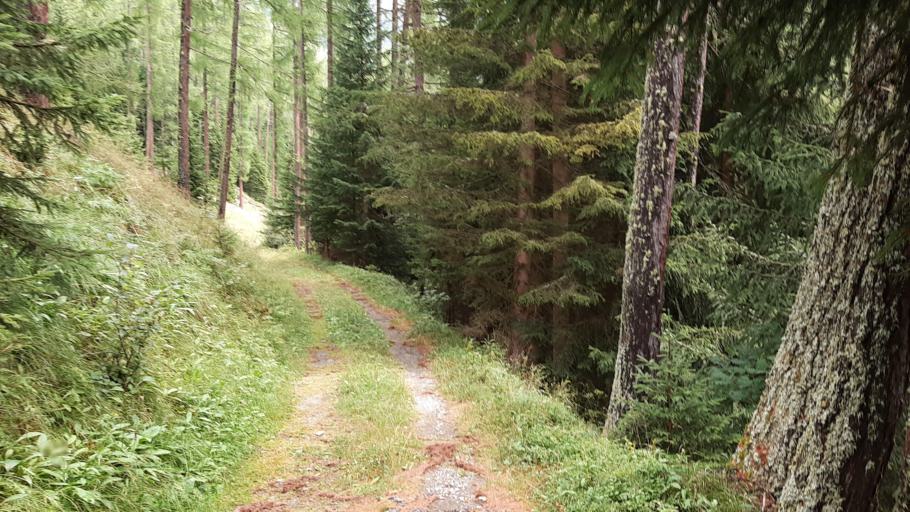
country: IT
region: Trentino-Alto Adige
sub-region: Bolzano
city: Sesto
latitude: 46.6965
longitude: 12.3765
